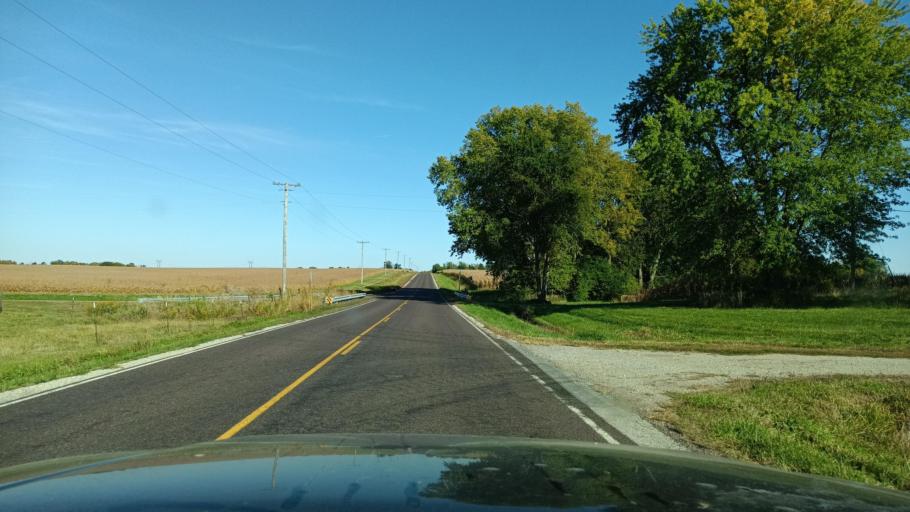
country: US
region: Illinois
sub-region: Logan County
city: Atlanta
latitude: 40.2386
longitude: -89.0966
